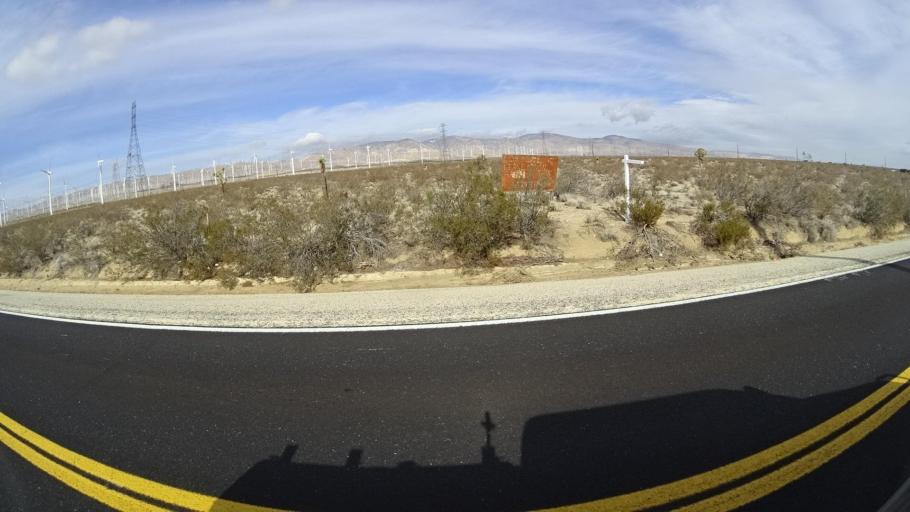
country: US
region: California
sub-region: Kern County
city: Mojave
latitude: 35.0492
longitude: -118.2055
